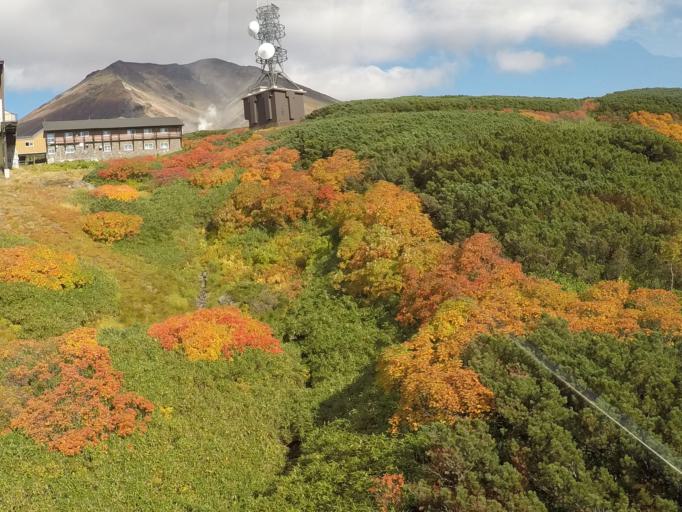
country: JP
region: Hokkaido
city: Kamikawa
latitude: 43.6615
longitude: 142.8238
